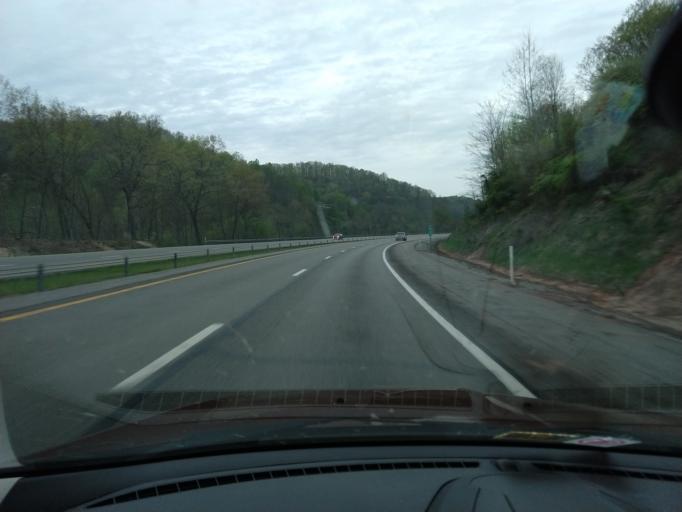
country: US
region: West Virginia
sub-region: Lewis County
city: Weston
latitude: 38.9925
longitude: -80.5063
